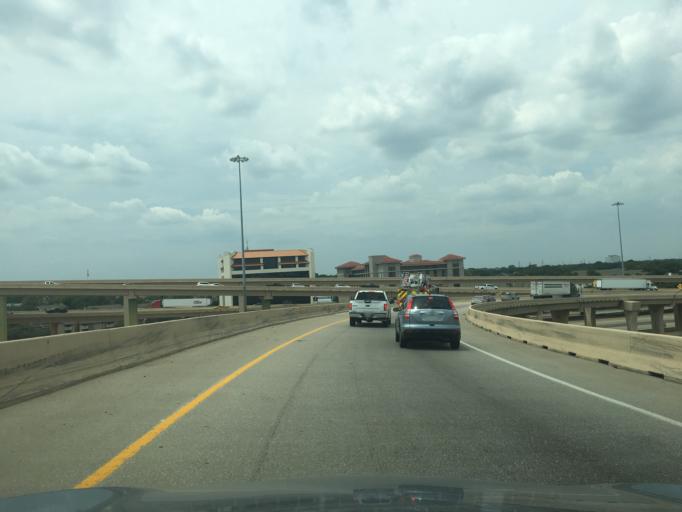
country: US
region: Texas
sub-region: Dallas County
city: Richardson
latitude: 32.9251
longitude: -96.7605
